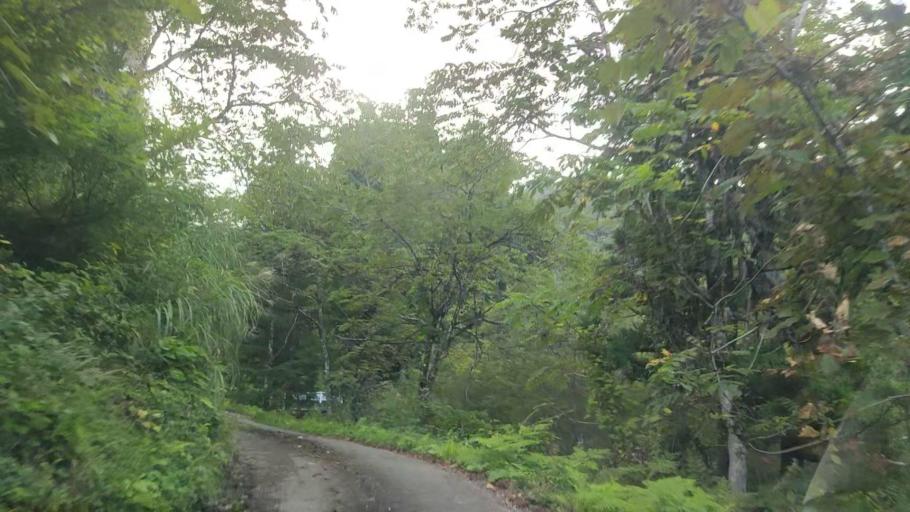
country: JP
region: Toyama
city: Yatsuomachi-higashikumisaka
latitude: 36.3299
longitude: 137.0772
